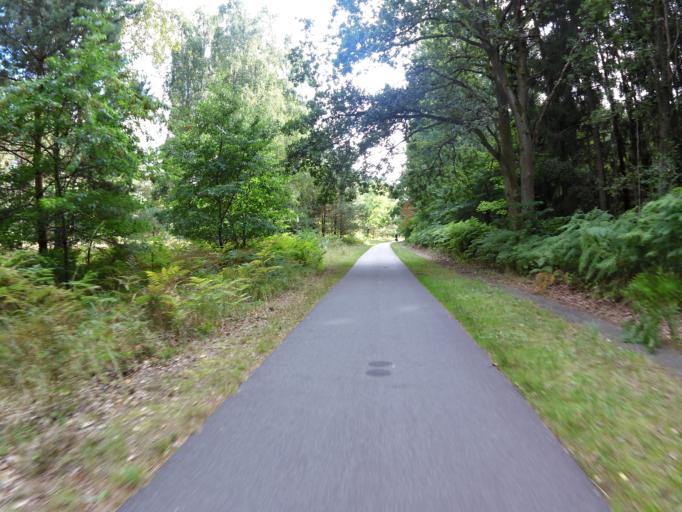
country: DE
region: Mecklenburg-Vorpommern
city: Karlshagen
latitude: 54.1405
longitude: 13.8139
